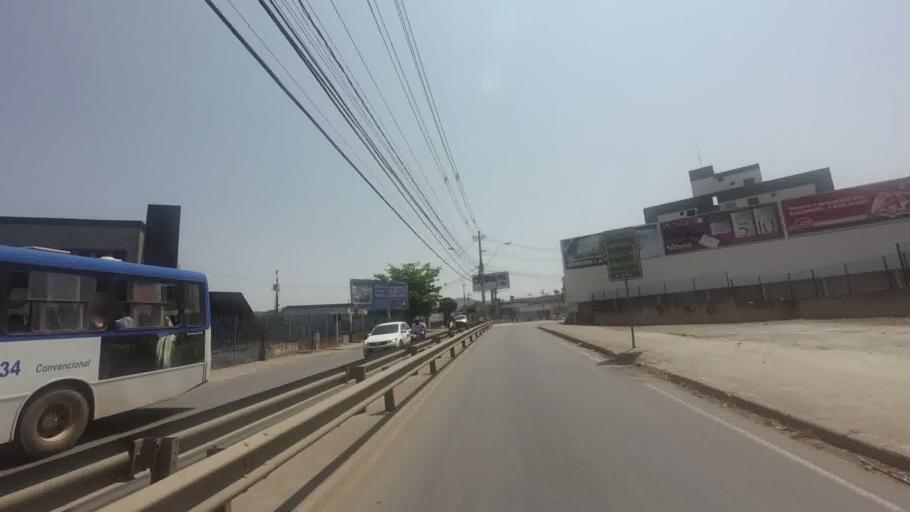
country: BR
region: Espirito Santo
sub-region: Cachoeiro De Itapemirim
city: Cachoeiro de Itapemirim
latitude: -20.8422
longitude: -41.1582
